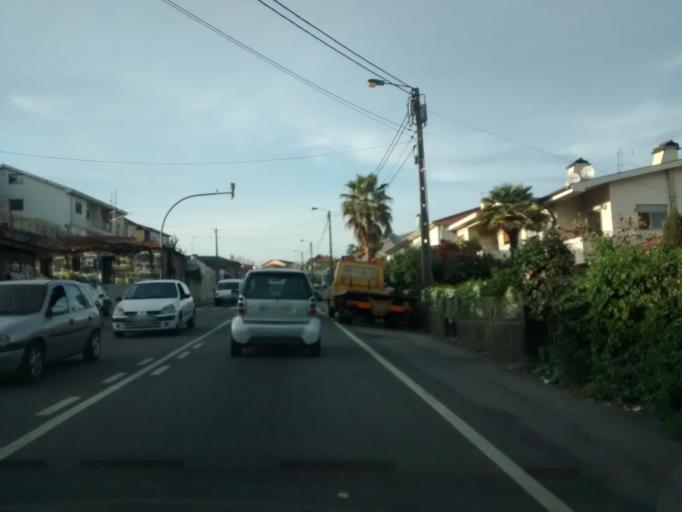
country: PT
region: Braga
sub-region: Guimaraes
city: Guimaraes
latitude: 41.4581
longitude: -8.3118
